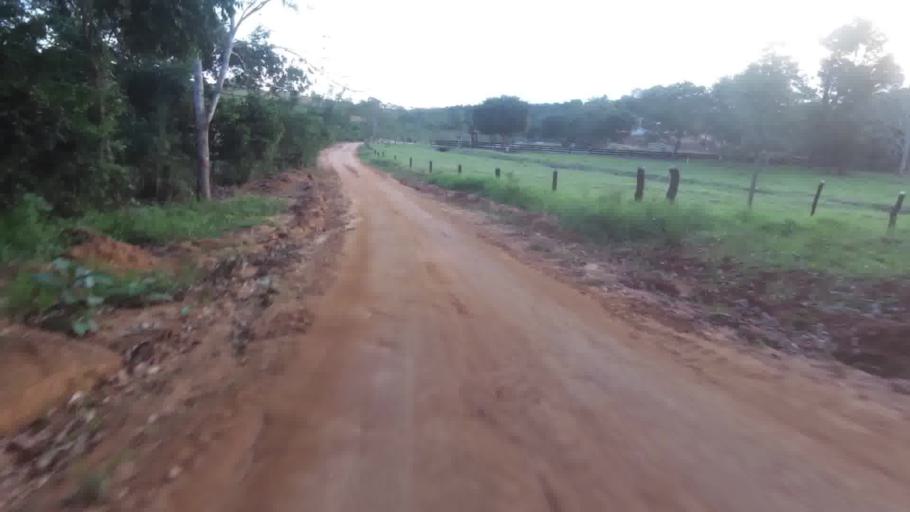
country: BR
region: Espirito Santo
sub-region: Guarapari
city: Guarapari
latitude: -20.6943
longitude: -40.5725
